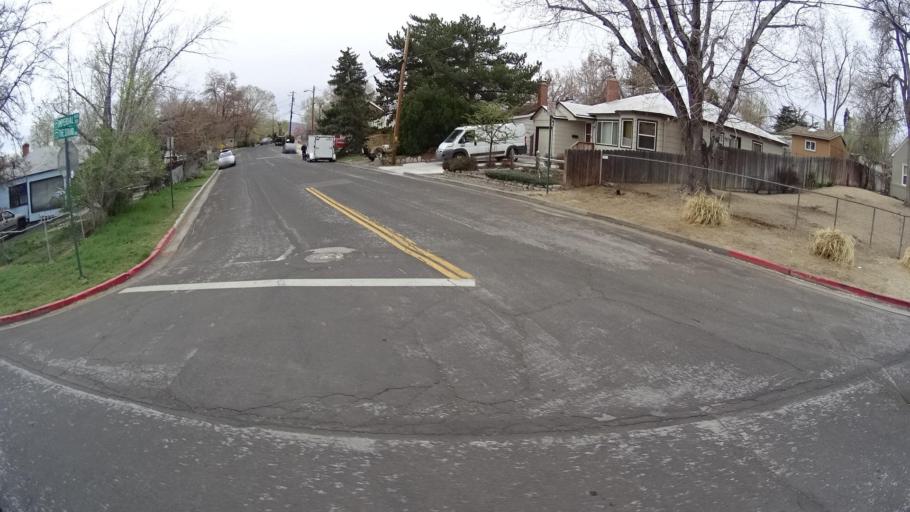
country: US
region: Nevada
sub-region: Washoe County
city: Reno
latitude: 39.5399
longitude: -119.8228
